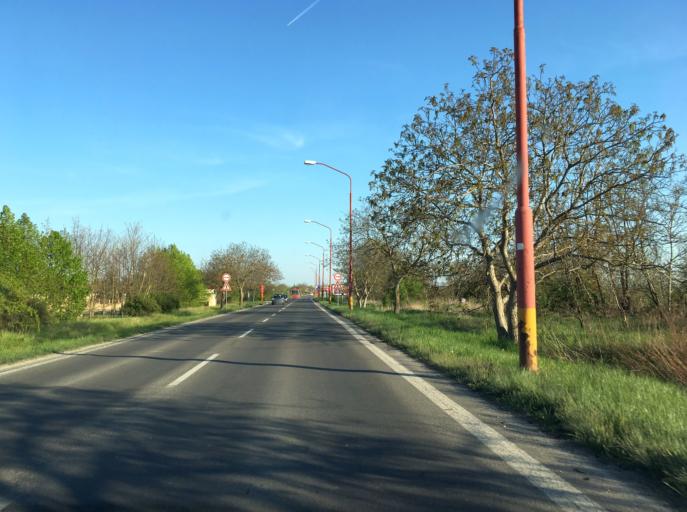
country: HU
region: Gyor-Moson-Sopron
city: Rajka
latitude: 48.0393
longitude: 17.1600
